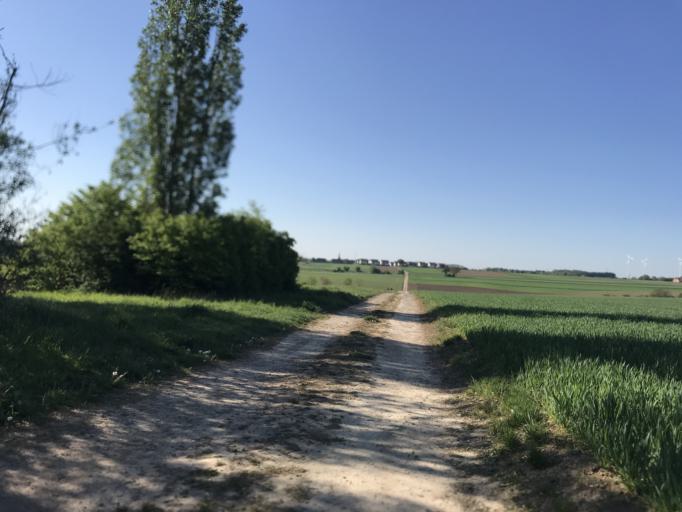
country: DE
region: Rheinland-Pfalz
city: Harxheim
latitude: 49.9247
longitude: 8.2405
